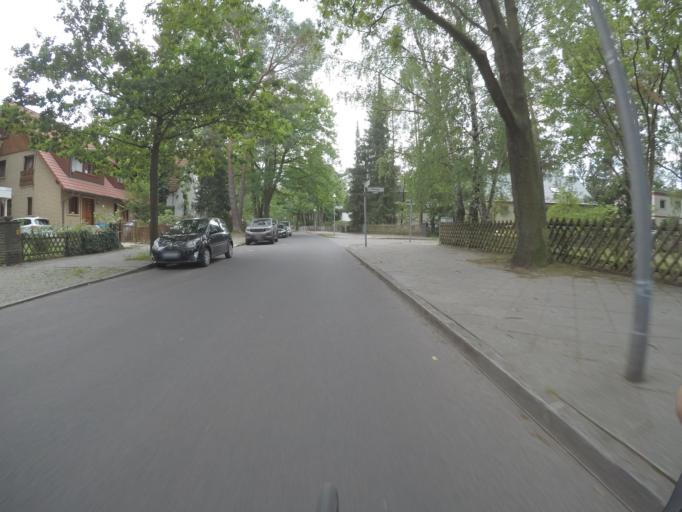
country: DE
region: Berlin
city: Frohnau
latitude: 52.6283
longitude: 13.2664
